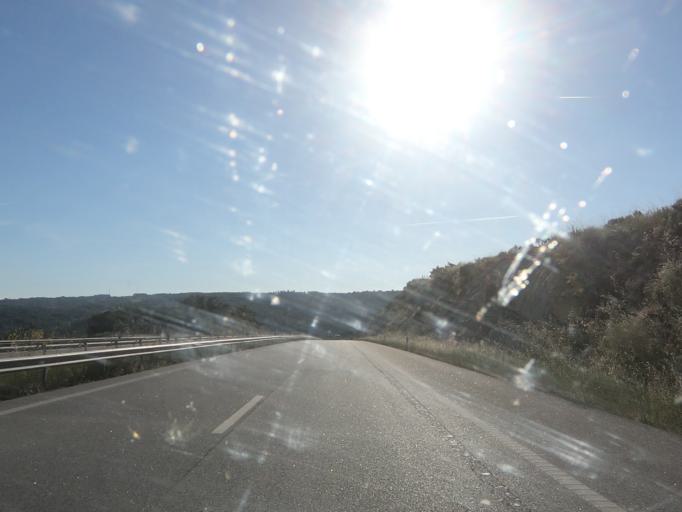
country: ES
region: Castille and Leon
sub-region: Provincia de Salamanca
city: Fuentes de Onoro
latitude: 40.6111
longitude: -6.9060
